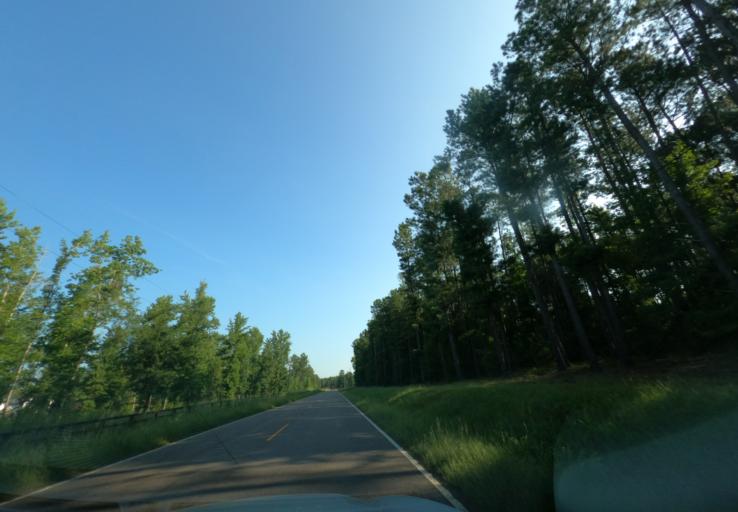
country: US
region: South Carolina
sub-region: Edgefield County
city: Murphys Estates
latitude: 33.6297
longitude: -81.9733
